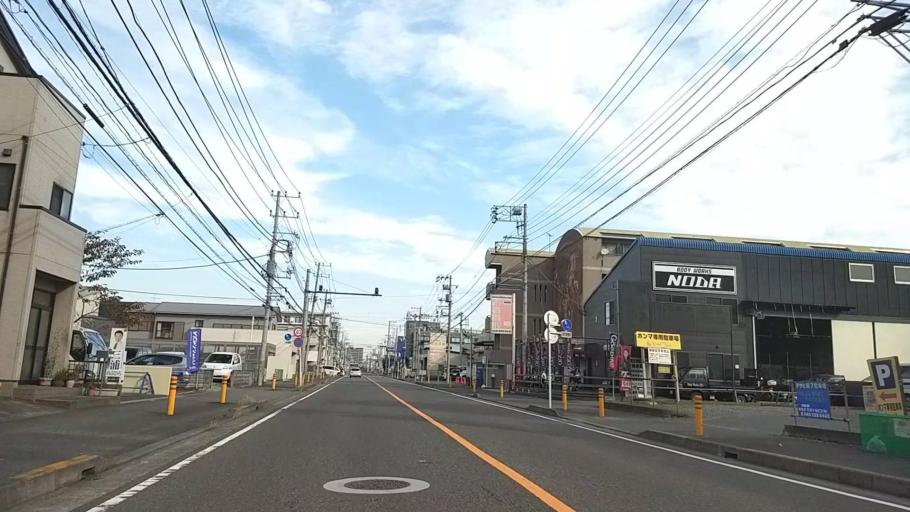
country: JP
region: Kanagawa
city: Atsugi
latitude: 35.4249
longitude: 139.3654
